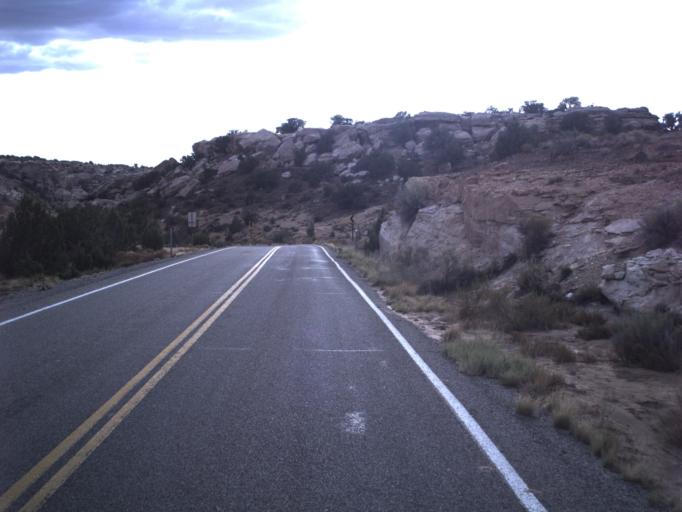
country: US
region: Utah
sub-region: San Juan County
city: Blanding
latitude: 37.4362
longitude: -109.3913
